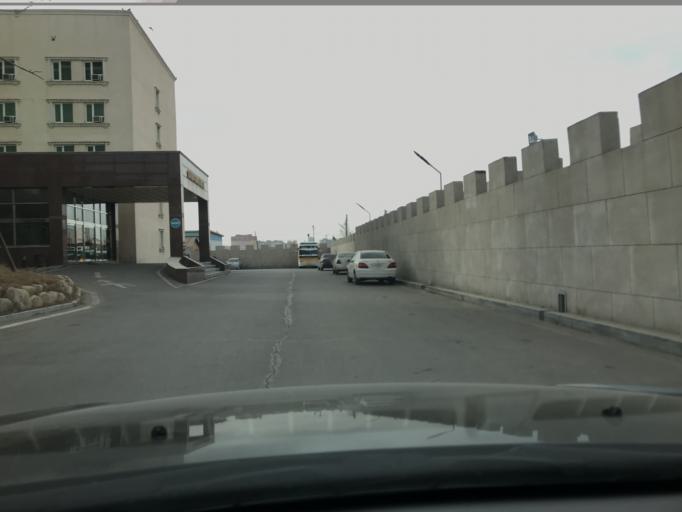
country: MN
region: Ulaanbaatar
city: Ulaanbaatar
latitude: 47.9133
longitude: 106.9733
